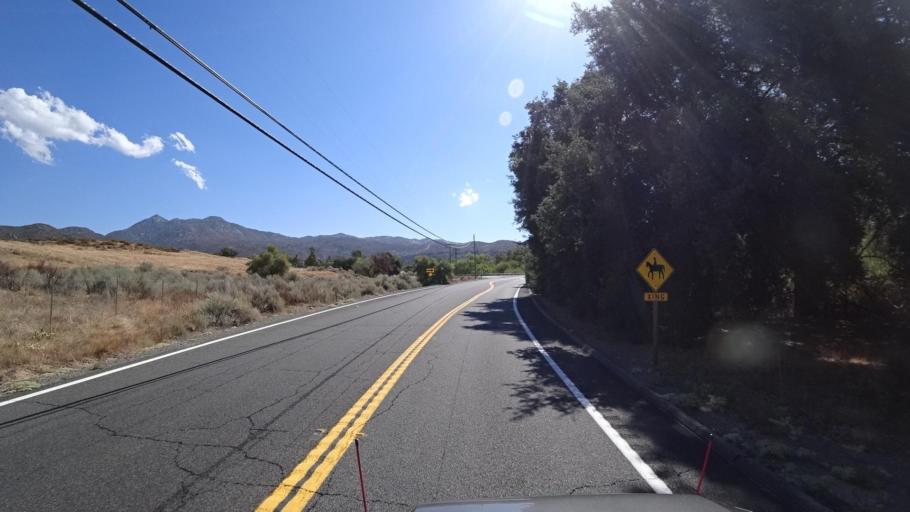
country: US
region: California
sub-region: San Diego County
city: Julian
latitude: 33.2854
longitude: -116.6367
